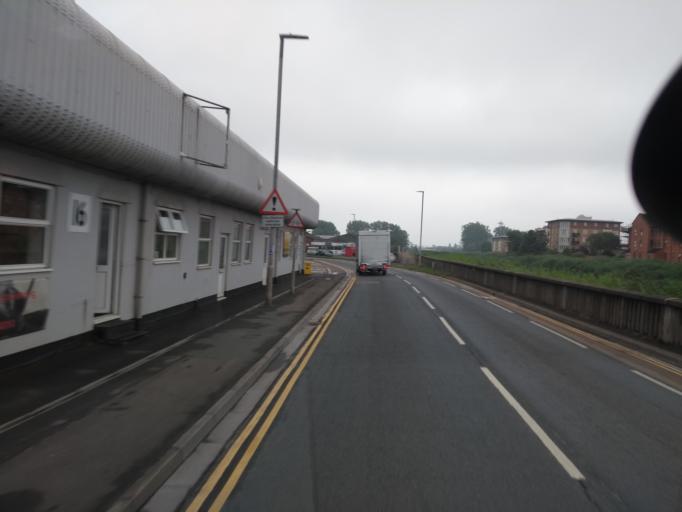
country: GB
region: England
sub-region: Somerset
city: Bridgwater
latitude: 51.1258
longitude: -2.9982
